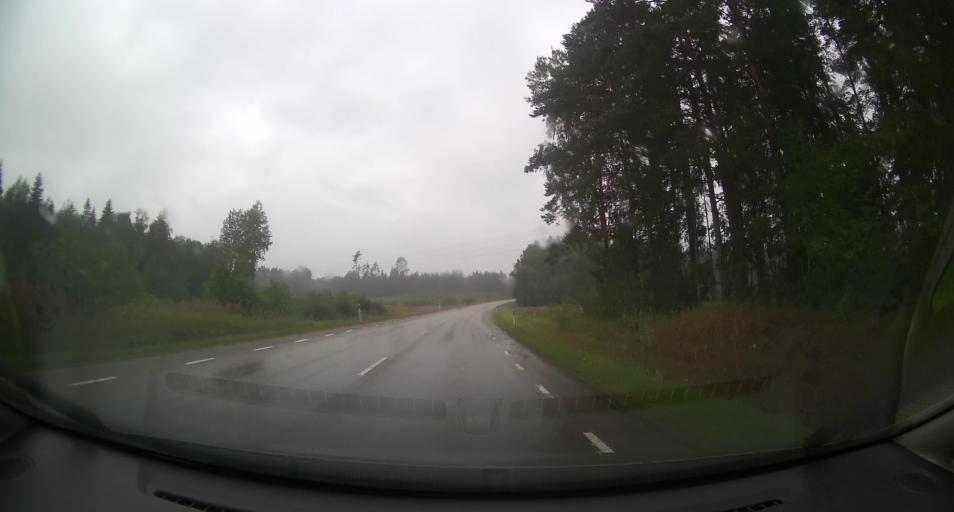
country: EE
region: Laeaene-Virumaa
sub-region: Viru-Nigula vald
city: Kunda
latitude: 59.3676
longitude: 26.6015
